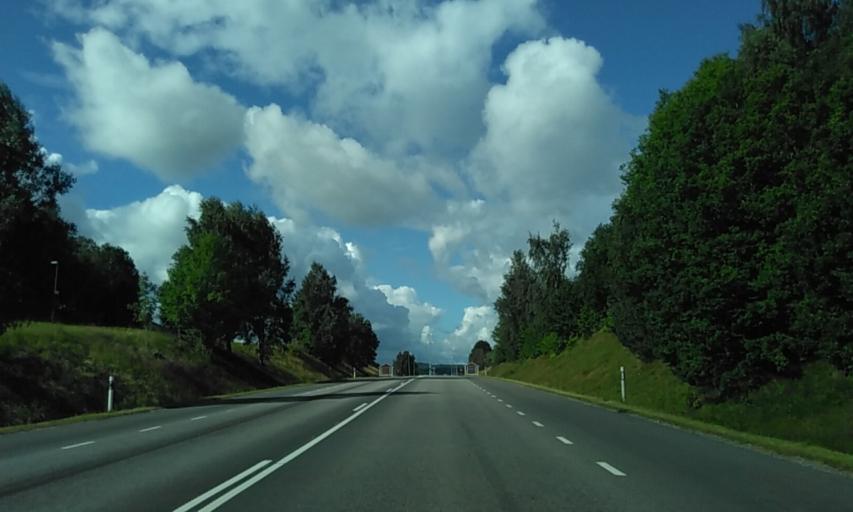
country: SE
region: Vaestra Goetaland
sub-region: Alingsas Kommun
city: Alingsas
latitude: 57.9392
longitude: 12.5536
